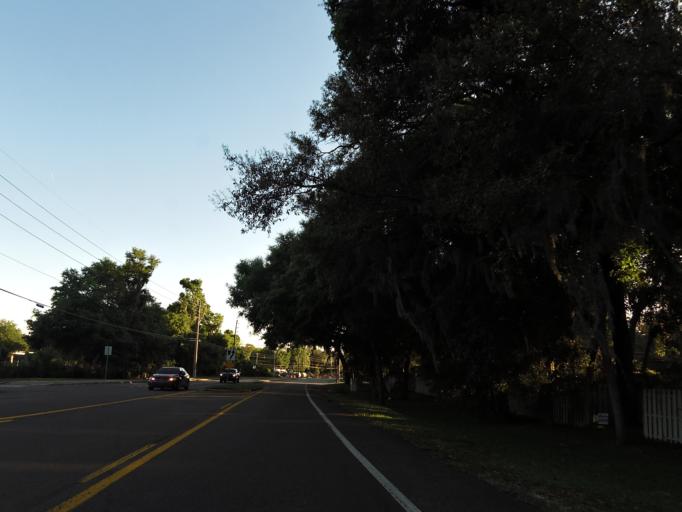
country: US
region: Florida
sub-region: Duval County
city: Atlantic Beach
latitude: 30.3590
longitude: -81.5169
